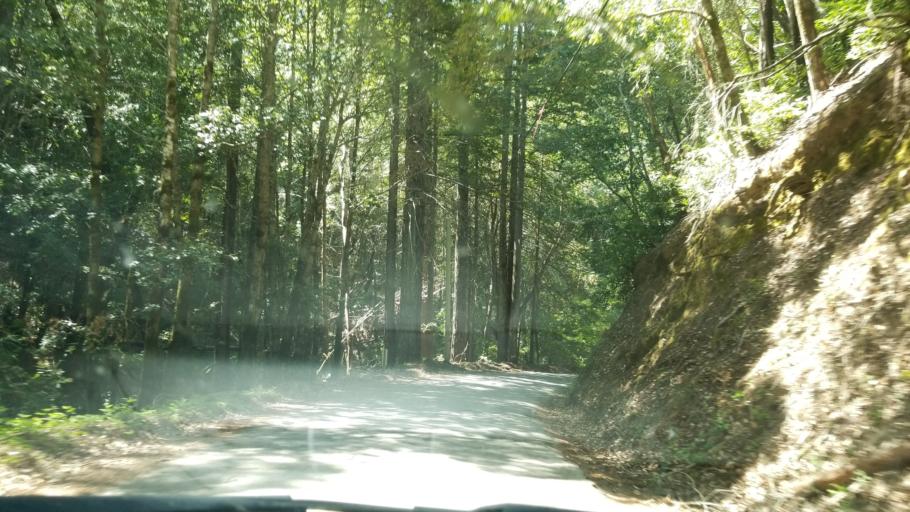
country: US
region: California
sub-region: Santa Cruz County
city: Day Valley
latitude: 37.0719
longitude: -121.8368
